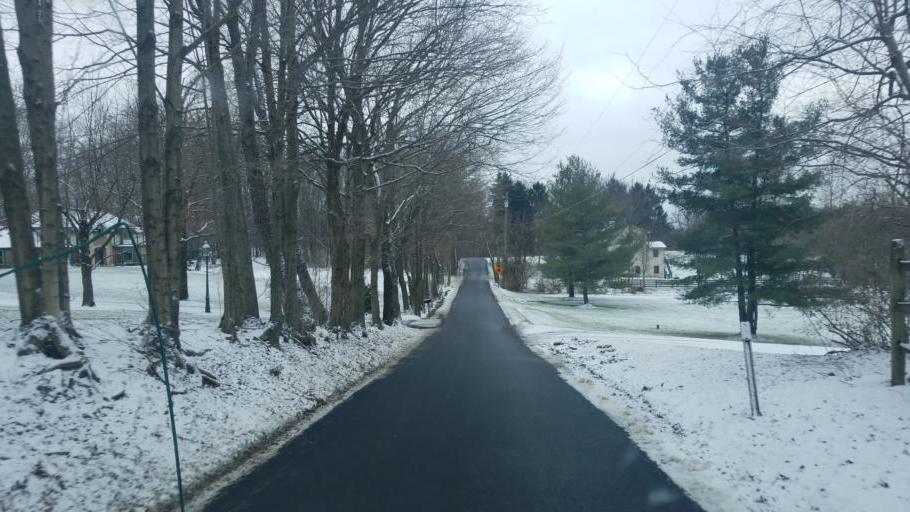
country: US
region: Ohio
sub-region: Franklin County
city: New Albany
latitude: 40.0317
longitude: -82.8174
